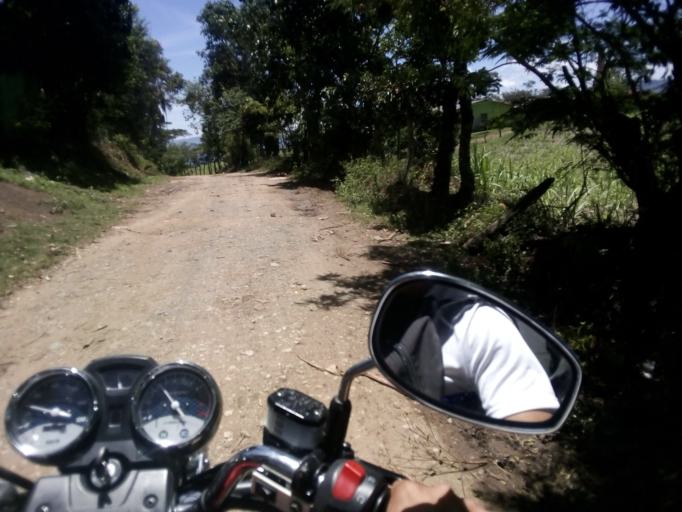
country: CO
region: Santander
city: Guepsa
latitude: 6.0083
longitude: -73.5566
